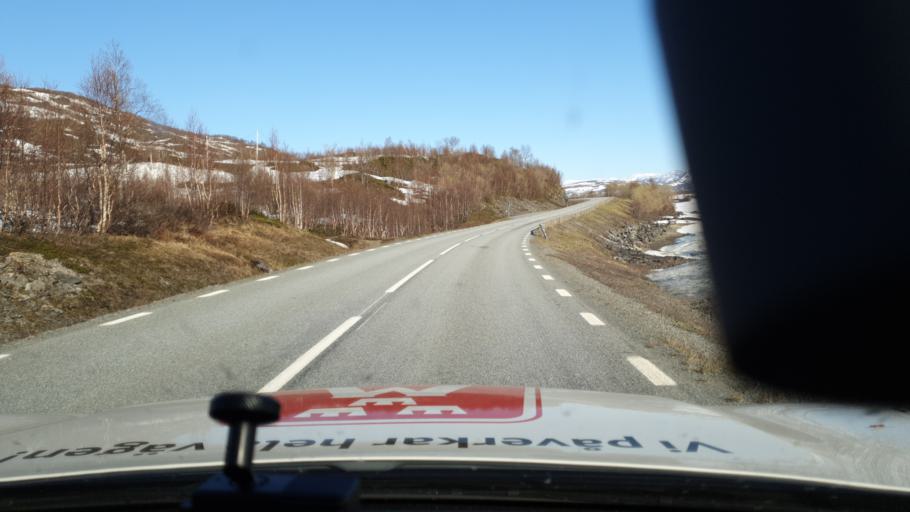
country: NO
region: Nordland
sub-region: Rana
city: Mo i Rana
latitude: 66.1287
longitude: 14.6490
